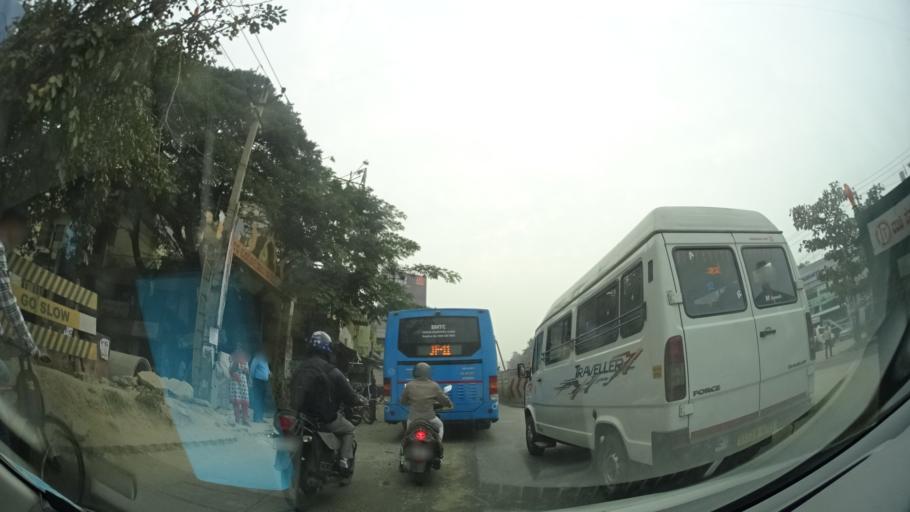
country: IN
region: Karnataka
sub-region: Bangalore Urban
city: Bangalore
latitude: 12.9963
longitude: 77.6936
